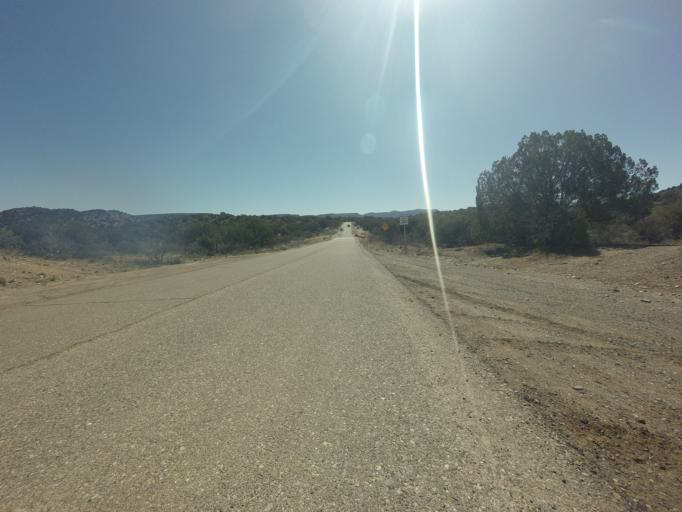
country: US
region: Arizona
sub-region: Yavapai County
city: Lake Montezuma
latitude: 34.6888
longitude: -111.7407
